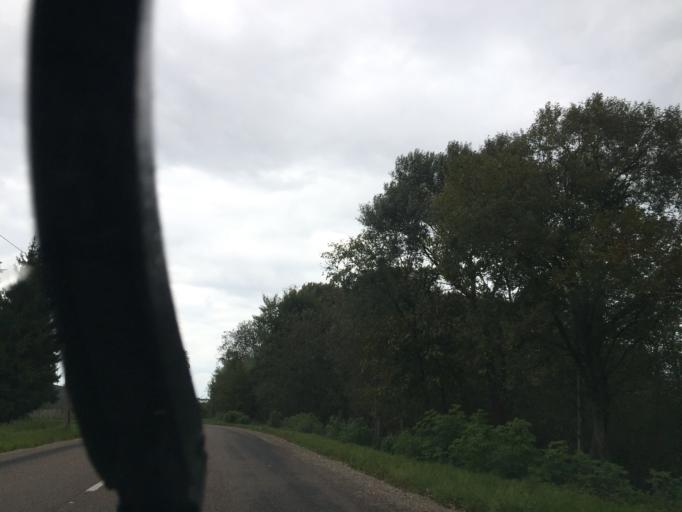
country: LV
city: Tireli
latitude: 56.7932
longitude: 23.6240
